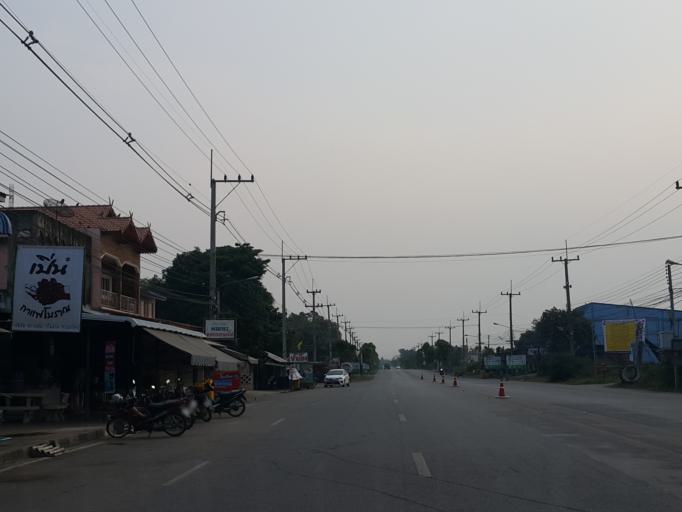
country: TH
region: Uthai Thani
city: Huai Khot
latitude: 15.1747
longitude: 99.6963
